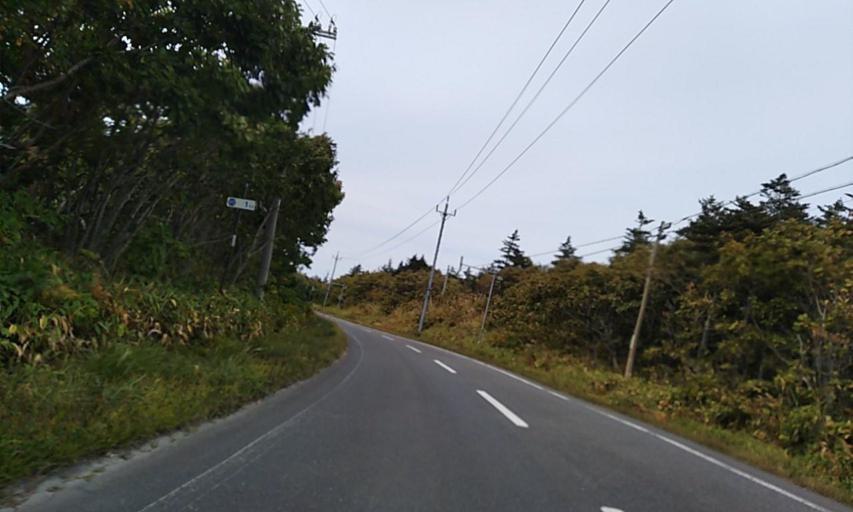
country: JP
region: Hokkaido
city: Makubetsu
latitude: 44.9983
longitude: 141.6962
